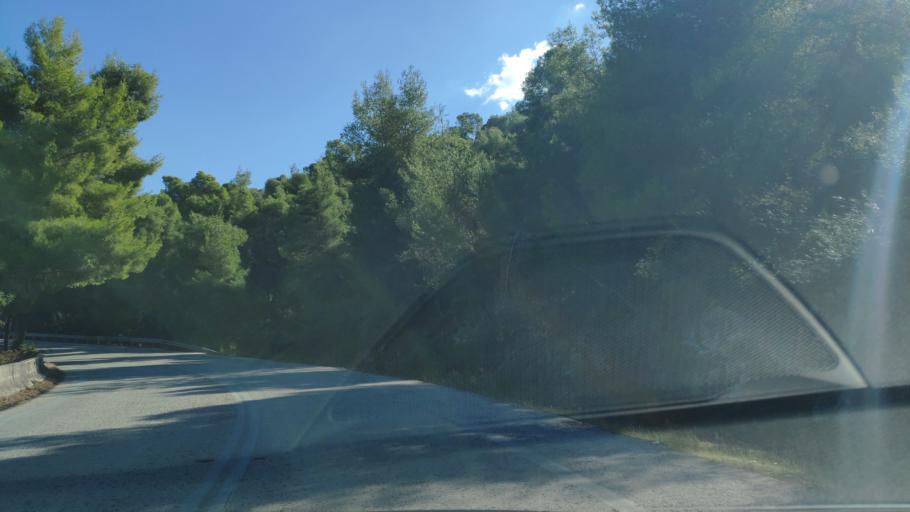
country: GR
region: Peloponnese
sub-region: Nomos Korinthias
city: Sofikon
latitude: 37.8288
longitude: 23.0488
